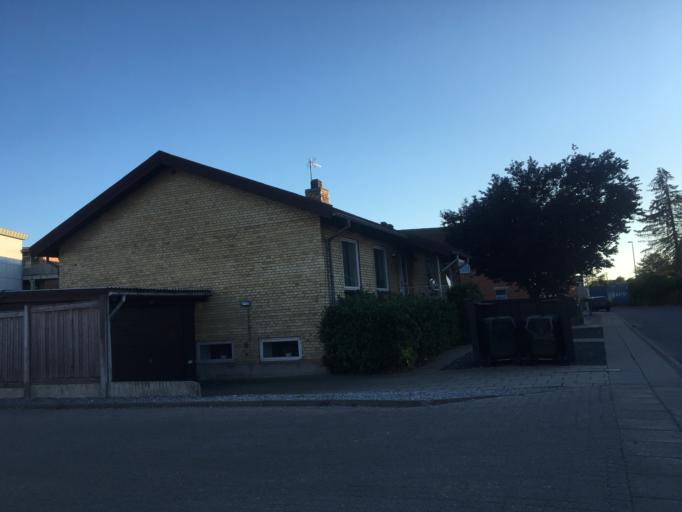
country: DK
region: Central Jutland
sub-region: Syddjurs Kommune
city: Hornslet
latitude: 56.3174
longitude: 10.3186
